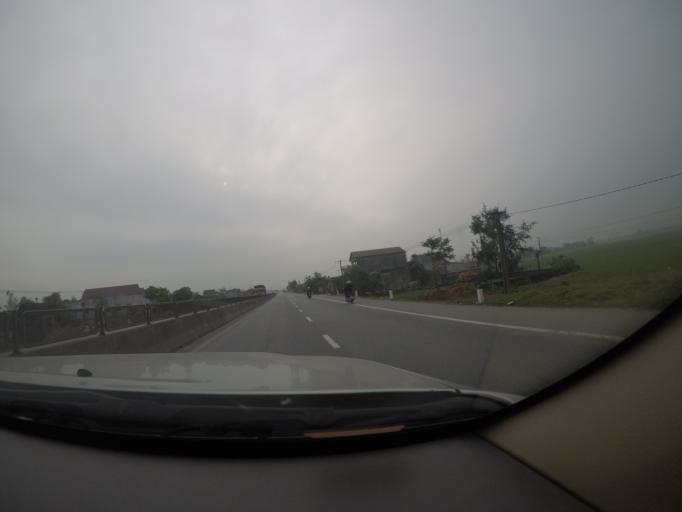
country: VN
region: Ha Tinh
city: Cam Xuyen
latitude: 18.2254
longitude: 106.0578
